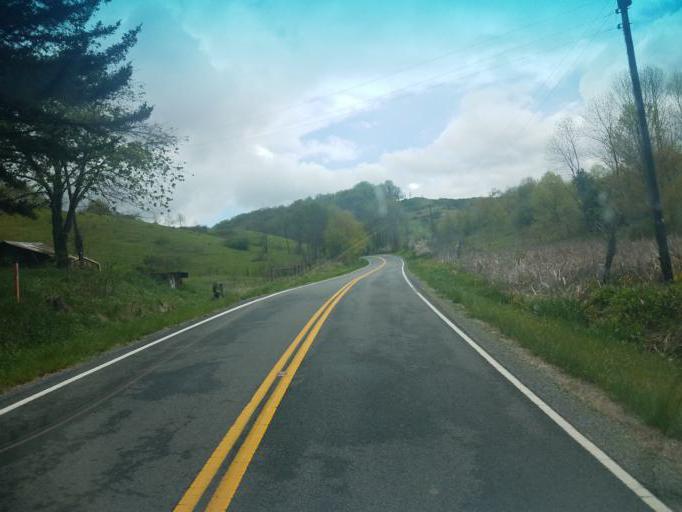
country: US
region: Virginia
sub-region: Smyth County
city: Atkins
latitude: 36.9863
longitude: -81.3914
